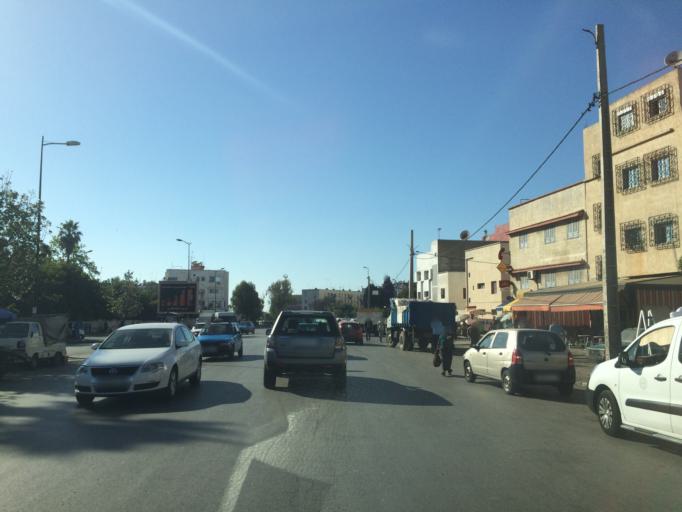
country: MA
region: Rabat-Sale-Zemmour-Zaer
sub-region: Rabat
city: Rabat
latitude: 33.9930
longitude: -6.8178
